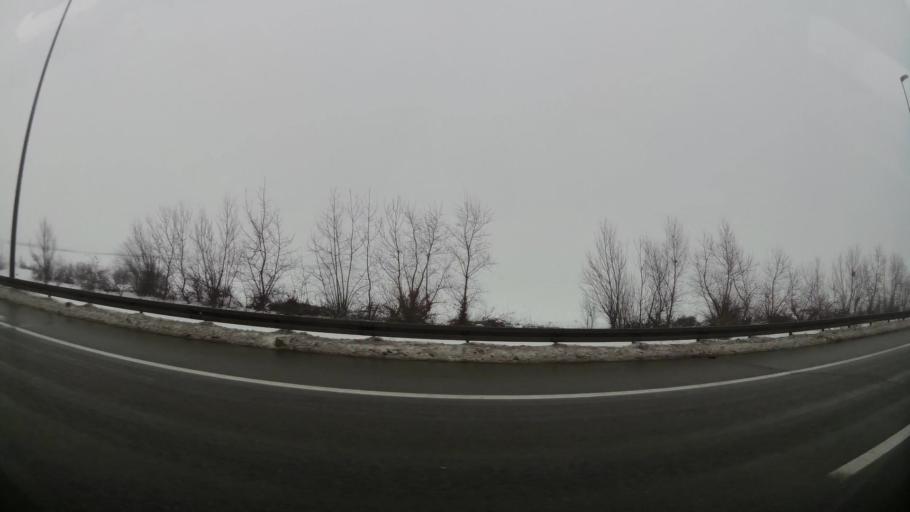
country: RS
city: Dobanovci
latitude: 44.8253
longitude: 20.2521
